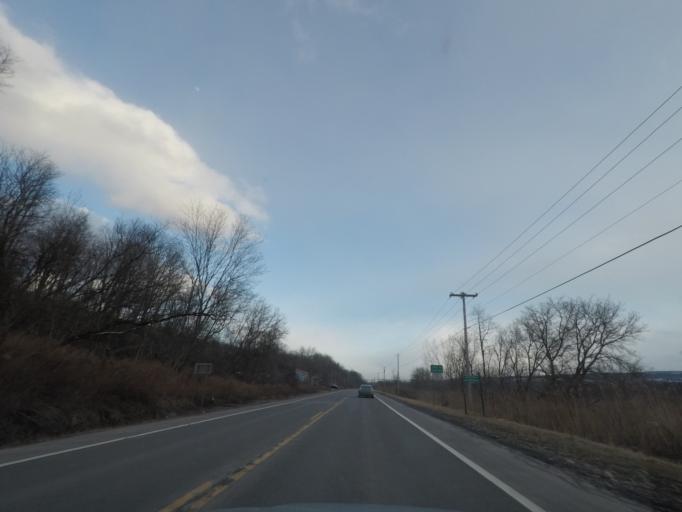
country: US
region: New York
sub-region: Herkimer County
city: Frankfort
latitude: 43.0346
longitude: -75.0511
